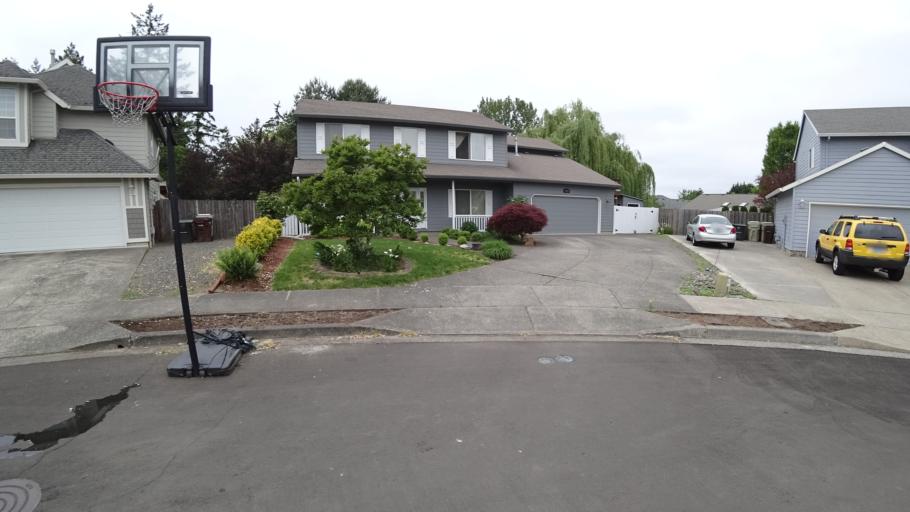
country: US
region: Oregon
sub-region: Washington County
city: Aloha
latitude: 45.5012
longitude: -122.9091
